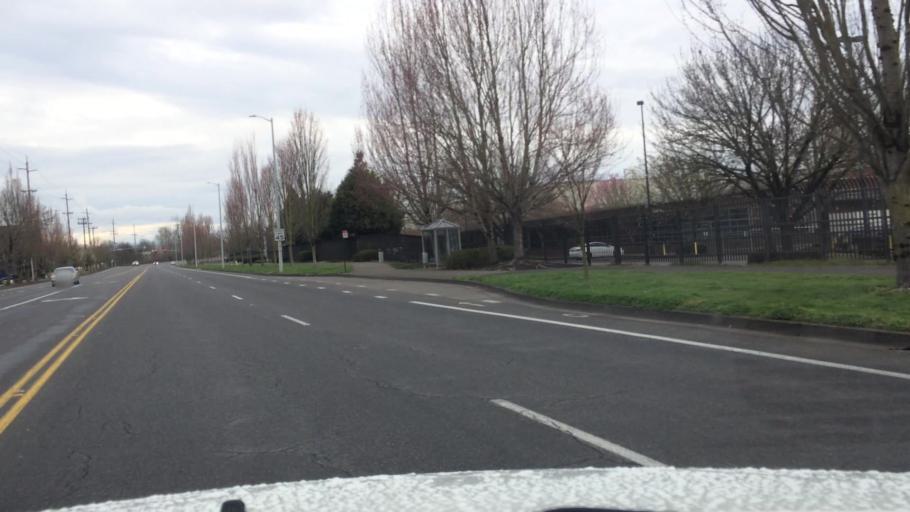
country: US
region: Oregon
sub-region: Marion County
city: Four Corners
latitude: 44.9280
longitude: -122.9939
